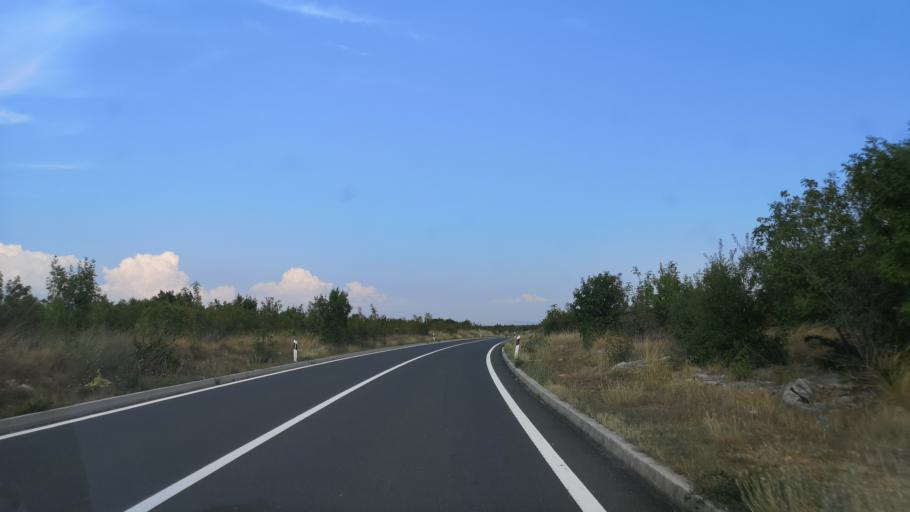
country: HR
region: Sibensko-Kniniska
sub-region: Grad Sibenik
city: Pirovac
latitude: 43.8817
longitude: 15.7587
